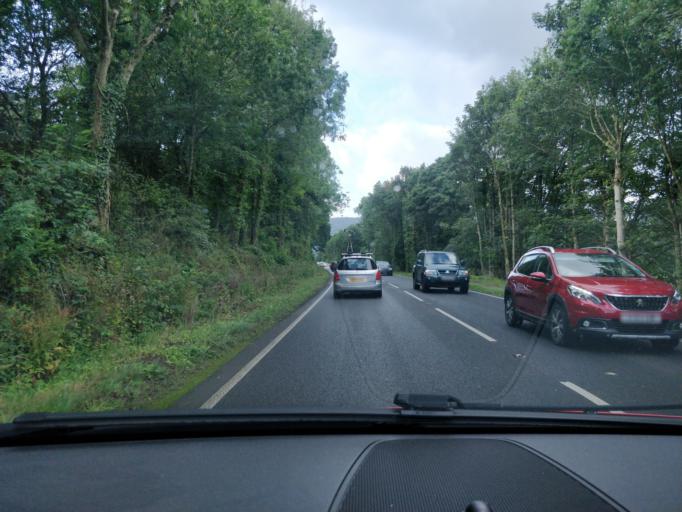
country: GB
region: Wales
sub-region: Conwy
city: Betws-y-Coed
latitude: 53.1072
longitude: -3.7847
